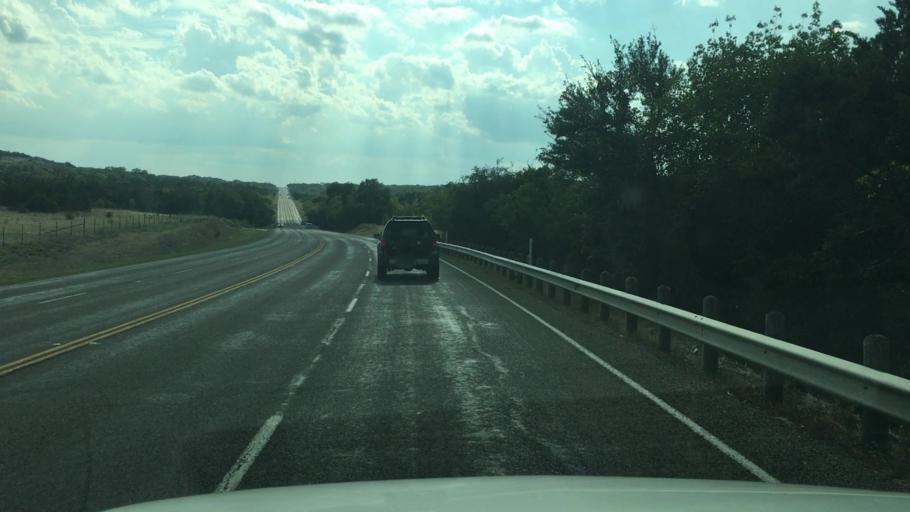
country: US
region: Texas
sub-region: Blanco County
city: Johnson City
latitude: 30.2111
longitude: -98.2810
